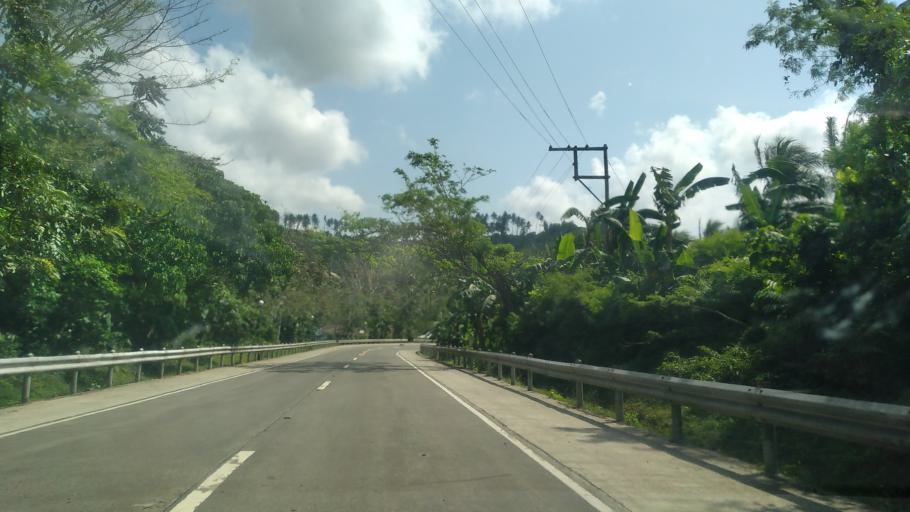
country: PH
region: Calabarzon
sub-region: Province of Quezon
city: Unisan
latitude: 13.8346
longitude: 122.0112
